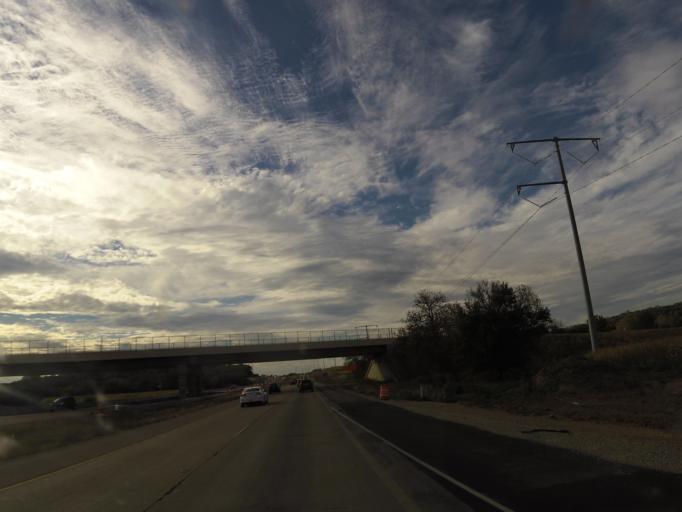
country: US
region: Wisconsin
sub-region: Dane County
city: Cottage Grove
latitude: 43.0047
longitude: -89.2090
